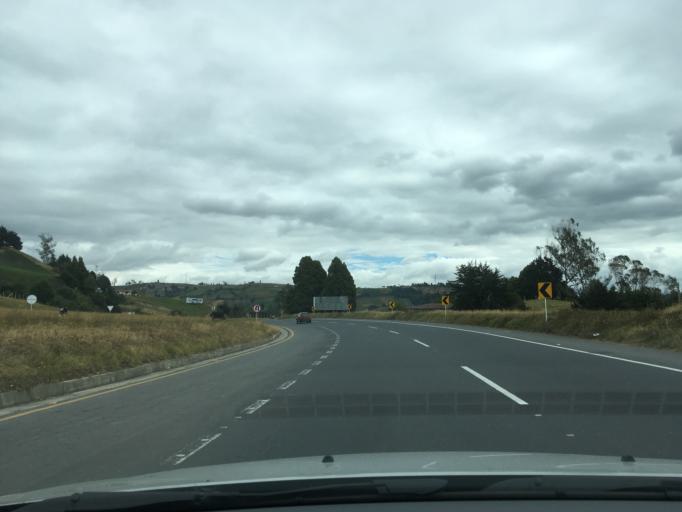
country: CO
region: Boyaca
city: Samaca
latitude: 5.4693
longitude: -73.4109
